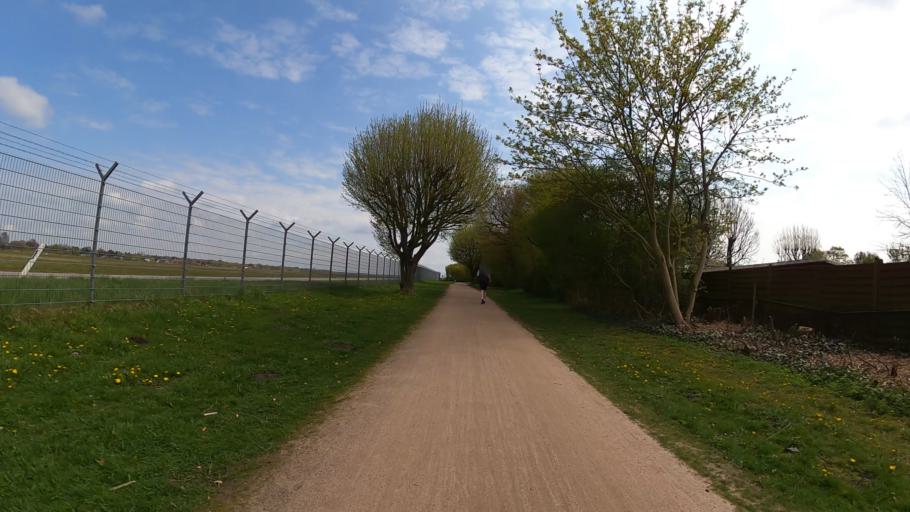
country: DE
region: Hamburg
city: Hamburg-Nord
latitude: 53.6154
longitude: 9.9620
